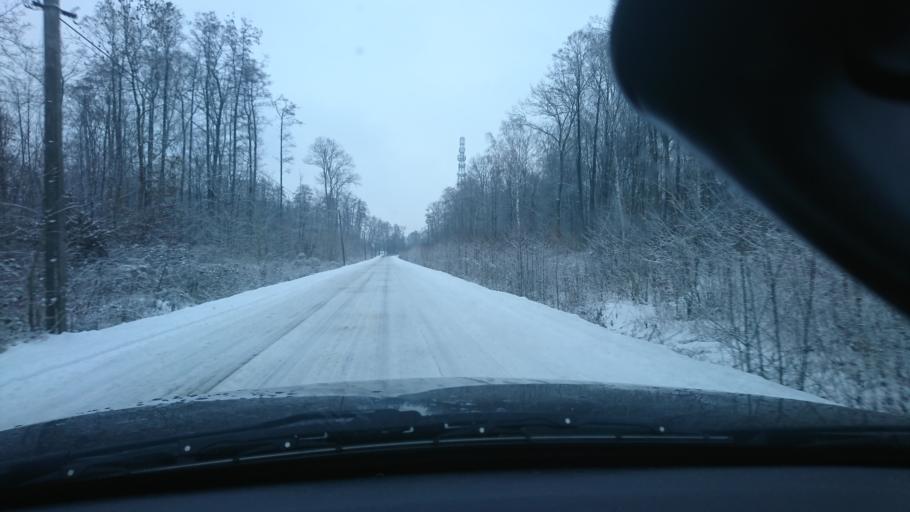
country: PL
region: Masovian Voivodeship
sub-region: Powiat ciechanowski
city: Glinojeck
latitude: 52.7499
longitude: 20.3111
